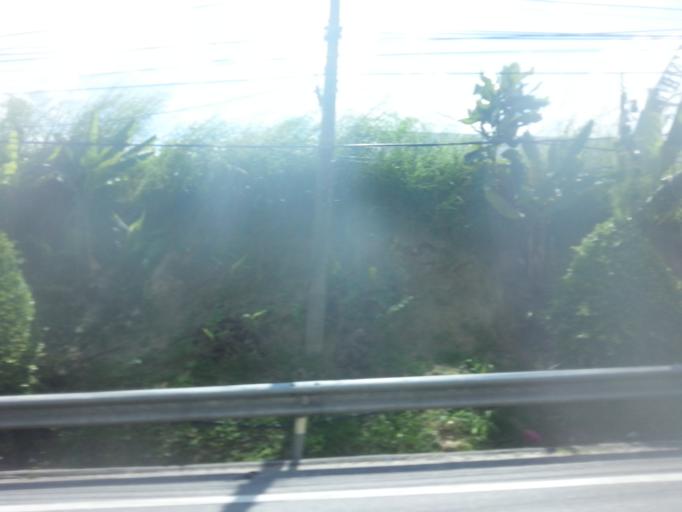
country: TH
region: Phuket
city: Patong
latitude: 7.9037
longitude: 98.3138
